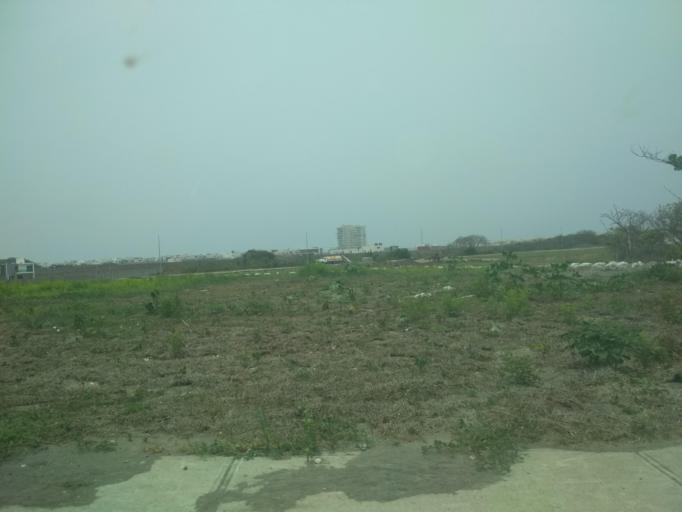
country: MX
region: Veracruz
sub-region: Alvarado
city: Playa de la Libertad
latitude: 19.0571
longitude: -96.0642
